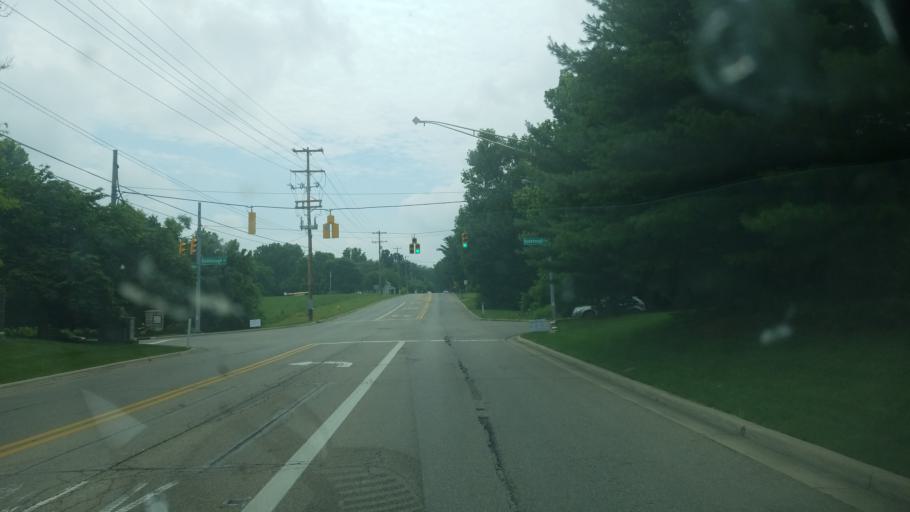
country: US
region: Ohio
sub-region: Franklin County
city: Reynoldsburg
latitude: 39.9744
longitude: -82.7932
